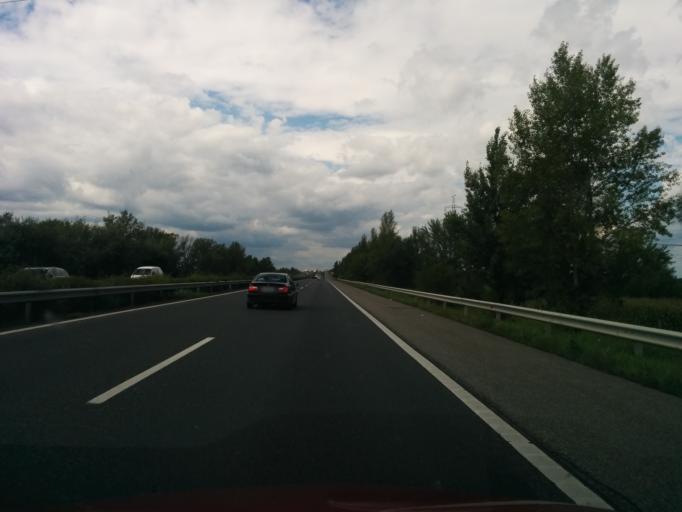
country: HU
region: Gyor-Moson-Sopron
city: Abda
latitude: 47.6604
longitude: 17.5855
